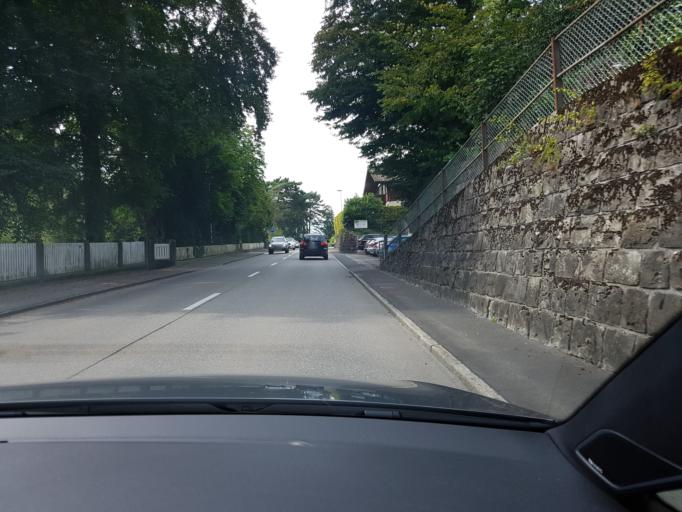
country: CH
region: Bern
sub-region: Thun District
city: Sigriswil
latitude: 46.7165
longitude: 7.6907
